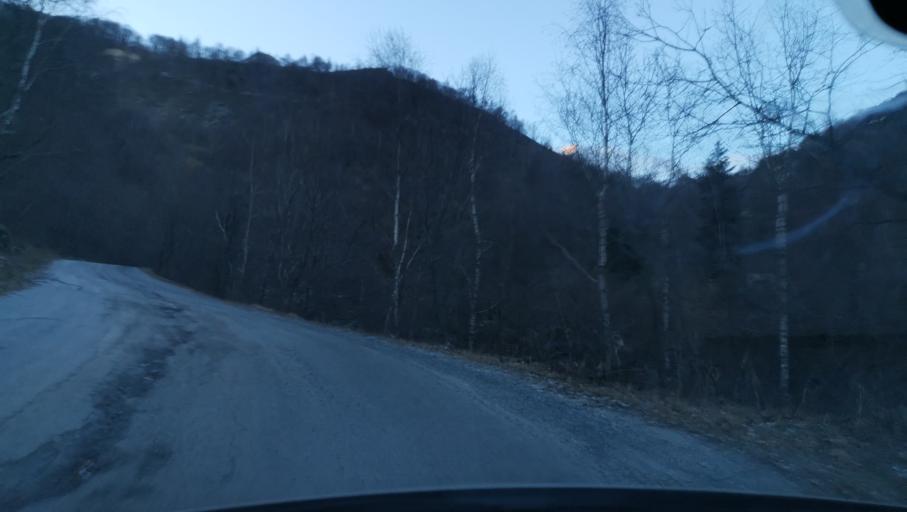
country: IT
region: Piedmont
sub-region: Provincia di Torino
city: Rora
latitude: 44.7686
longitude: 7.2038
